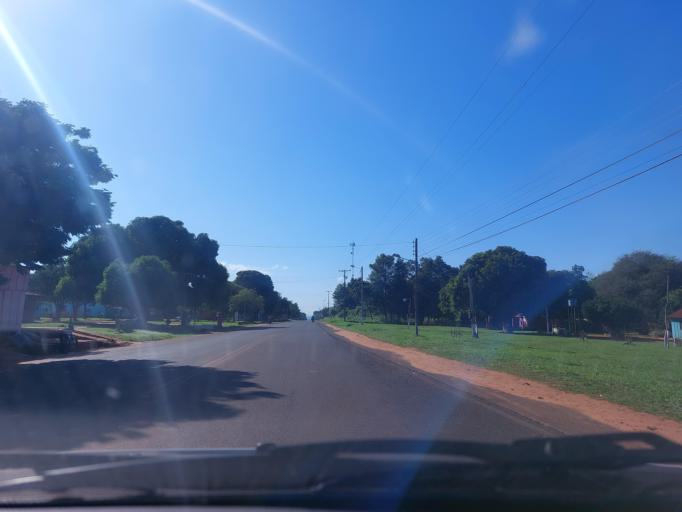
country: PY
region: San Pedro
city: Guayaybi
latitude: -24.5315
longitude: -56.4462
